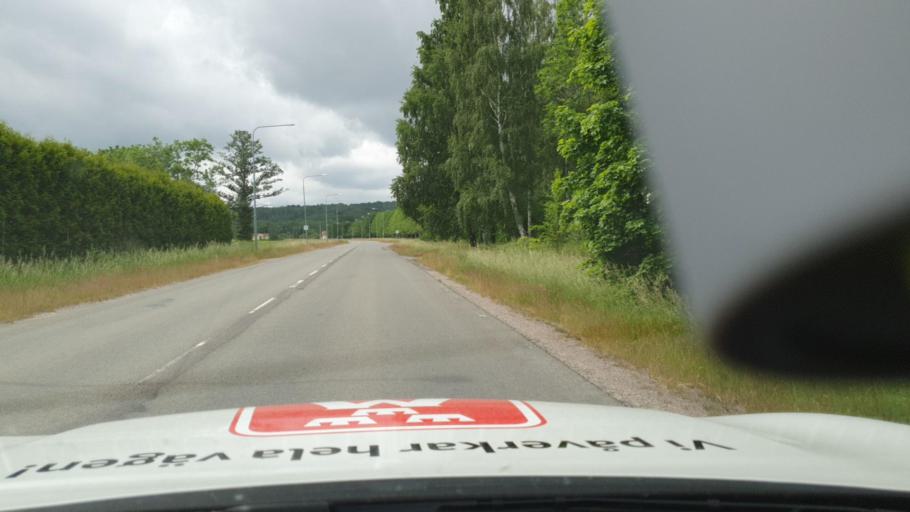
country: SE
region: Vaestra Goetaland
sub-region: Hjo Kommun
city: Hjo
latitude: 58.2909
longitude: 14.2761
